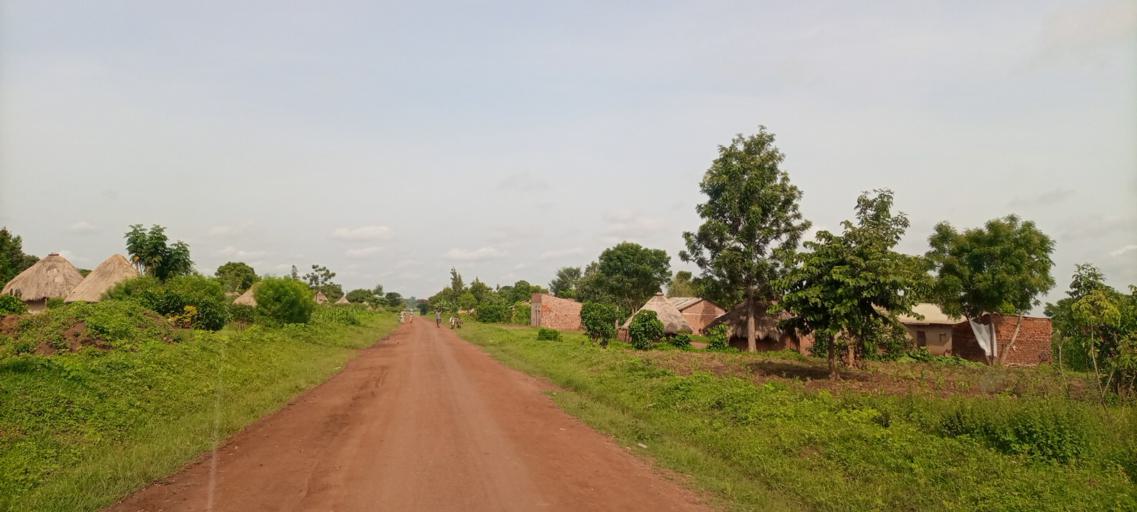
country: UG
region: Eastern Region
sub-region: Kibuku District
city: Kibuku
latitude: 1.1044
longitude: 33.7827
